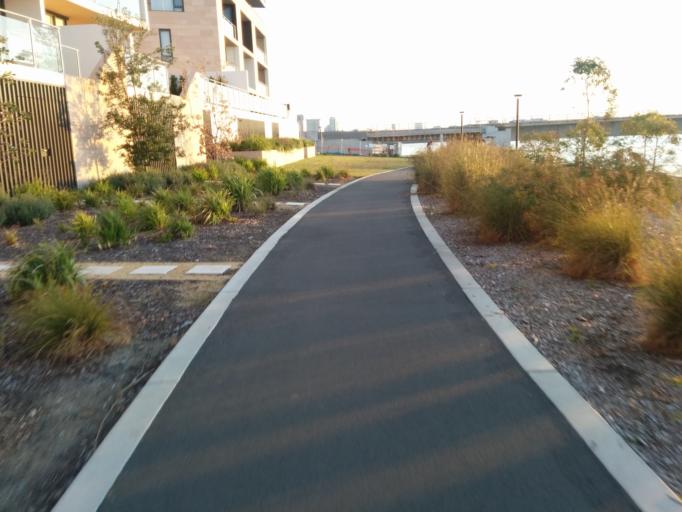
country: AU
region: New South Wales
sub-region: Canada Bay
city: Rhodes
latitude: -33.8273
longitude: 151.0838
